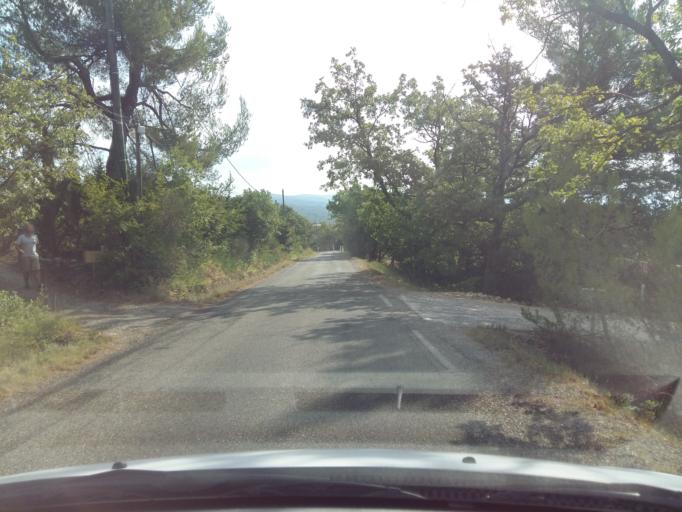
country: FR
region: Provence-Alpes-Cote d'Azur
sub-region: Departement du Vaucluse
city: Gordes
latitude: 43.9450
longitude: 5.2501
